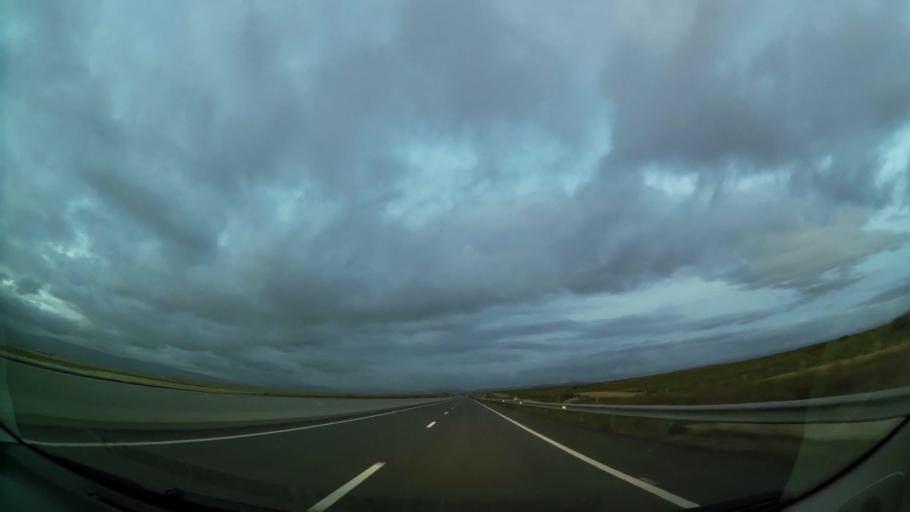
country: MA
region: Oriental
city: El Aioun
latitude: 34.6285
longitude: -2.3666
